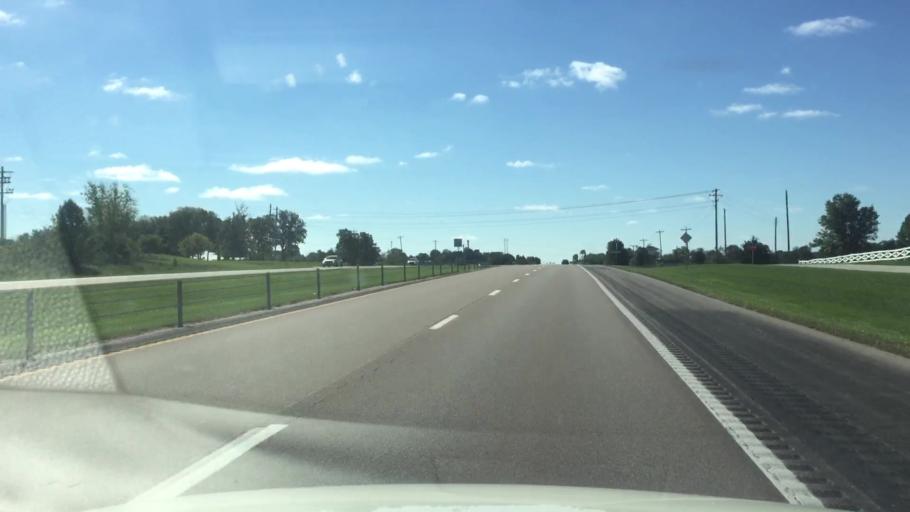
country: US
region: Missouri
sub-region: Boone County
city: Ashland
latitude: 38.7998
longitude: -92.2516
